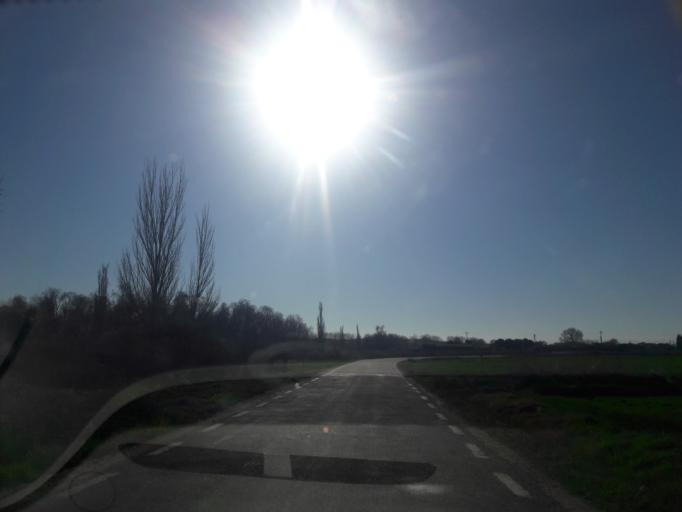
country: ES
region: Castille and Leon
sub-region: Provincia de Salamanca
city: Tordillos
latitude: 40.8586
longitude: -5.3579
